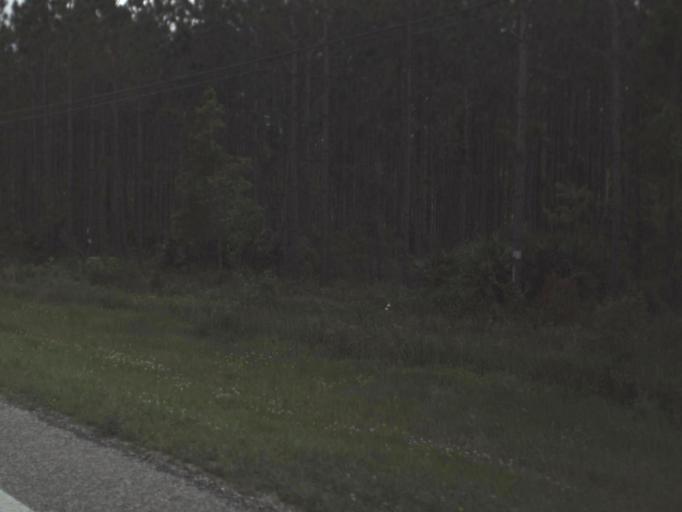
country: US
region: Florida
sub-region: Saint Johns County
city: Butler Beach
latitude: 29.7063
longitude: -81.2997
